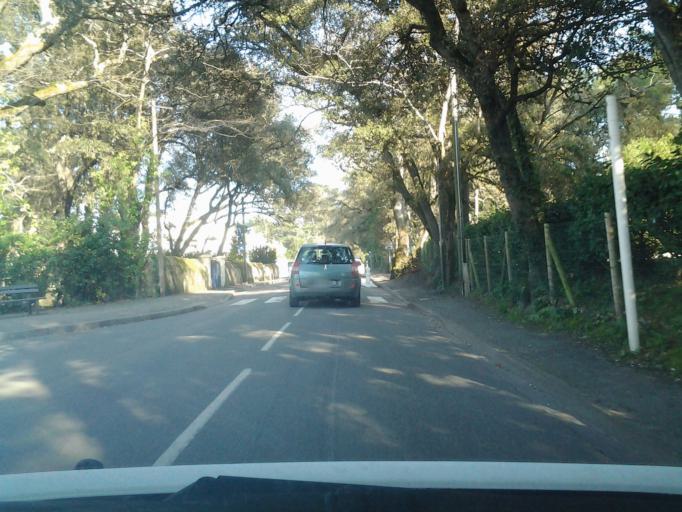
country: FR
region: Pays de la Loire
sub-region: Departement de la Vendee
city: La Gueriniere
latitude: 47.0078
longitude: -2.2312
